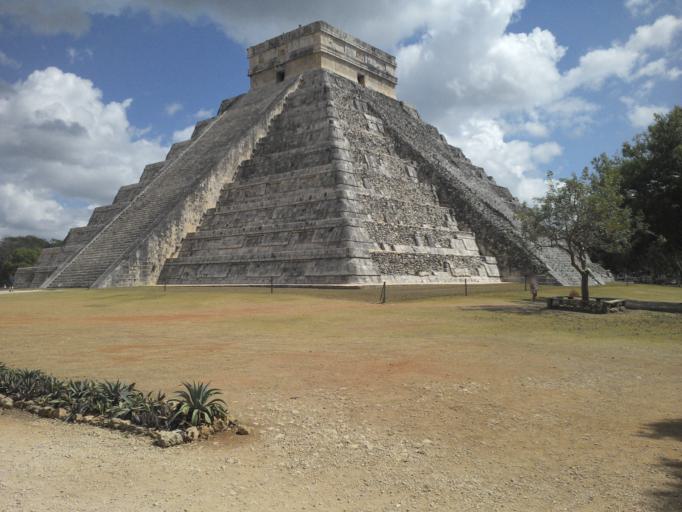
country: MX
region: Yucatan
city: Chichen-Itza
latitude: 20.6827
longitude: -88.5694
